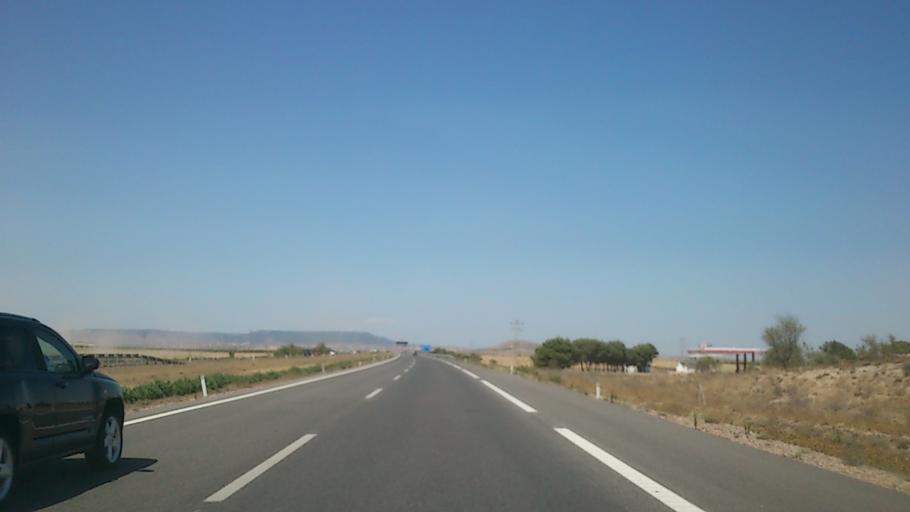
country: ES
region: Aragon
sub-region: Provincia de Zaragoza
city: Gallur
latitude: 41.8441
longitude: -1.3531
